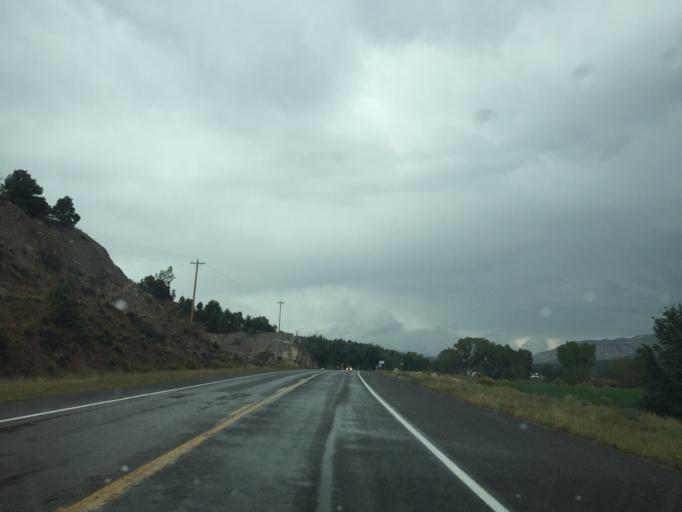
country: US
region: Utah
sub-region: Kane County
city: Kanab
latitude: 37.2385
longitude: -112.6732
